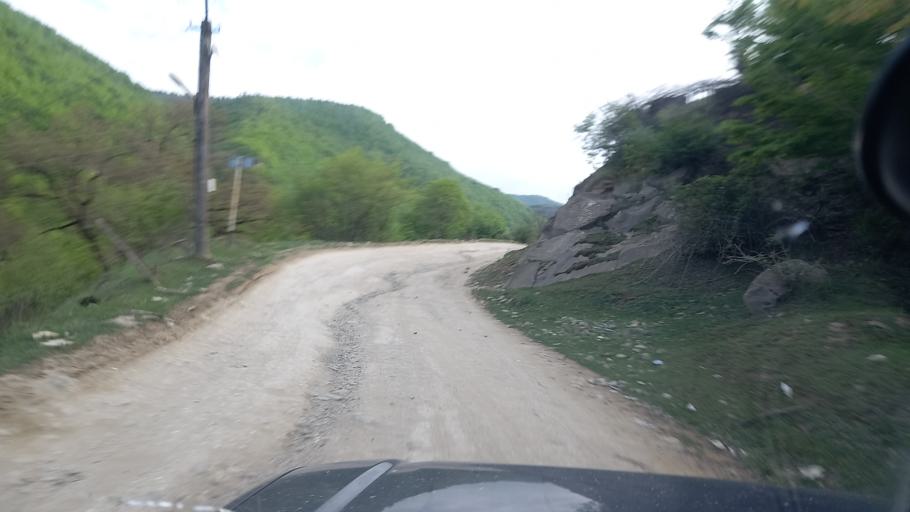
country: RU
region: Dagestan
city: Khuchni
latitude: 41.9699
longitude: 47.8770
